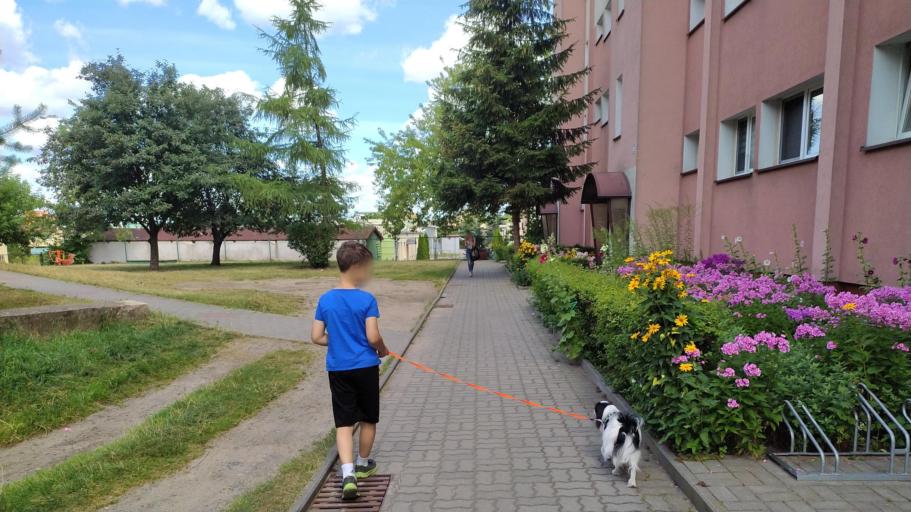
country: PL
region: Warmian-Masurian Voivodeship
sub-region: Powiat ilawski
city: Ilawa
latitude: 53.5897
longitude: 19.5621
